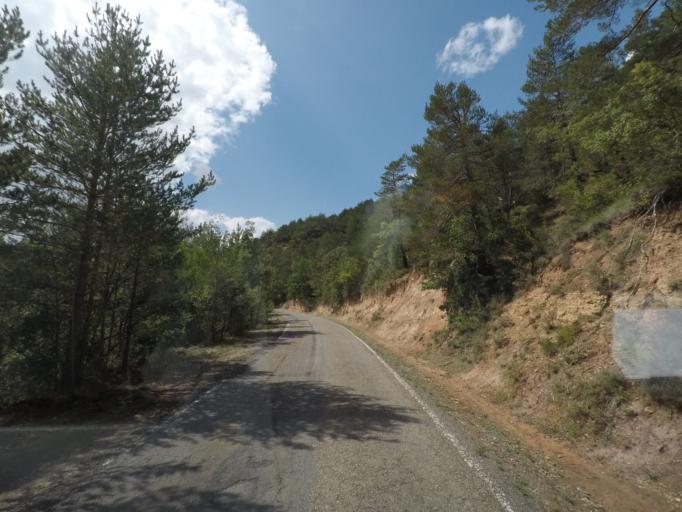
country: ES
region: Aragon
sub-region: Provincia de Huesca
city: Yebra de Basa
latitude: 42.4069
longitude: -0.2308
